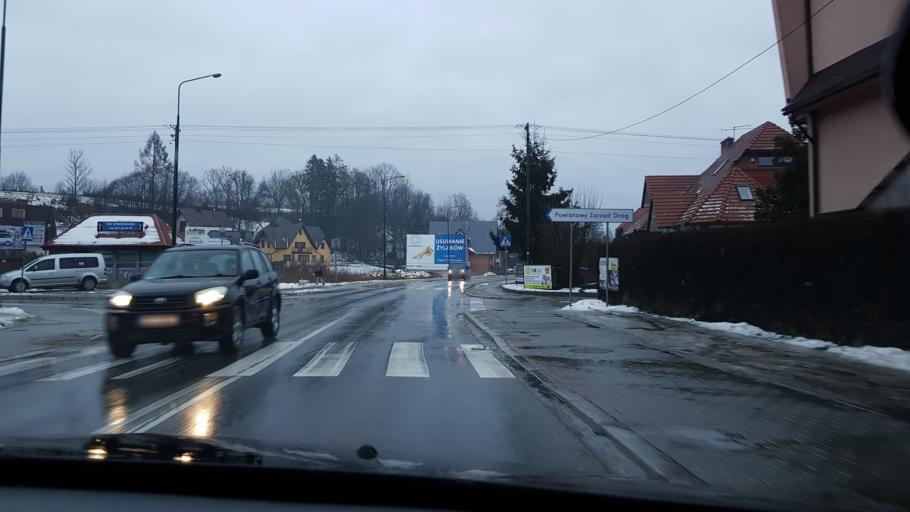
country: PL
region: Lesser Poland Voivodeship
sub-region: Powiat nowotarski
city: Nowy Targ
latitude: 49.4860
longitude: 20.0332
